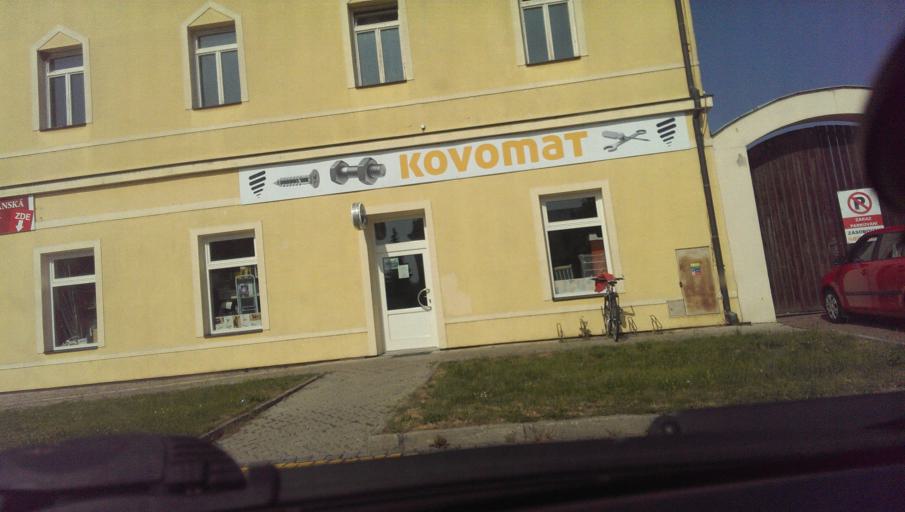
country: CZ
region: Zlin
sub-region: Okres Uherske Hradiste
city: Uherske Hradiste
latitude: 49.0687
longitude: 17.4638
